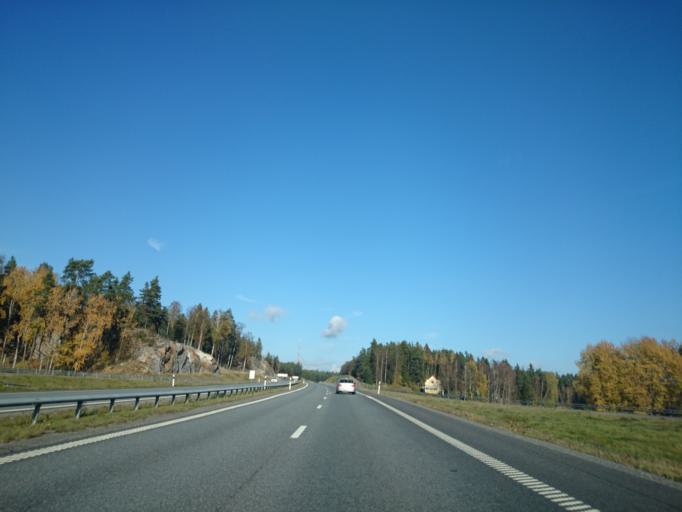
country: SE
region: Stockholm
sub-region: Haninge Kommun
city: Jordbro
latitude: 59.0689
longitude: 18.0644
